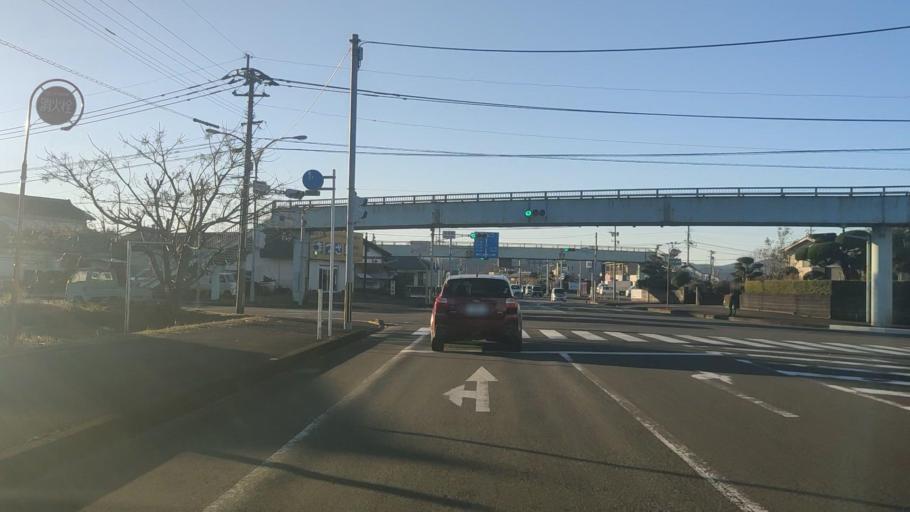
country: JP
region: Miyazaki
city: Miyazaki-shi
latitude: 31.8320
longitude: 131.3002
